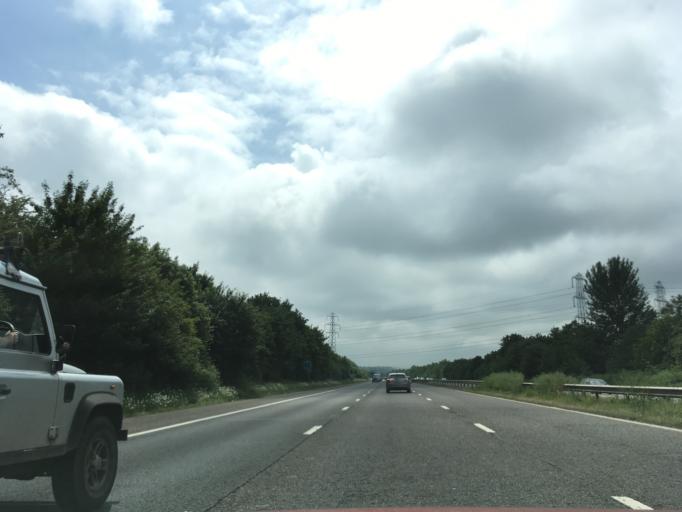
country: GB
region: England
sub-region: Devon
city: Cullompton
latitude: 50.8772
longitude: -3.3811
